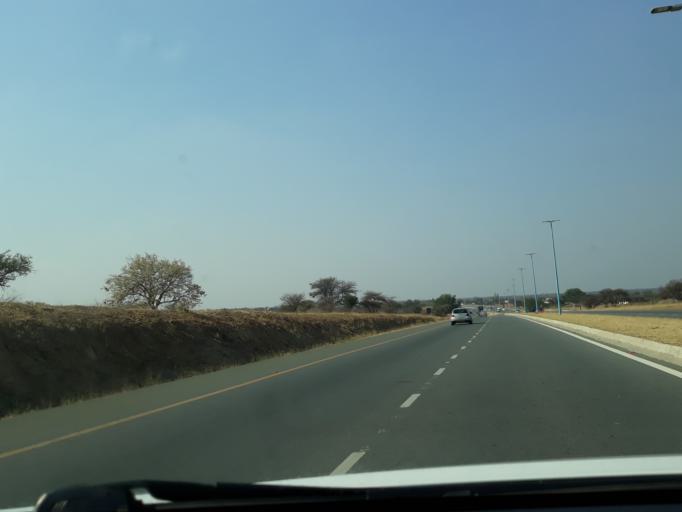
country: BW
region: Central
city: Tonota
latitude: -21.4132
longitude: 27.4490
